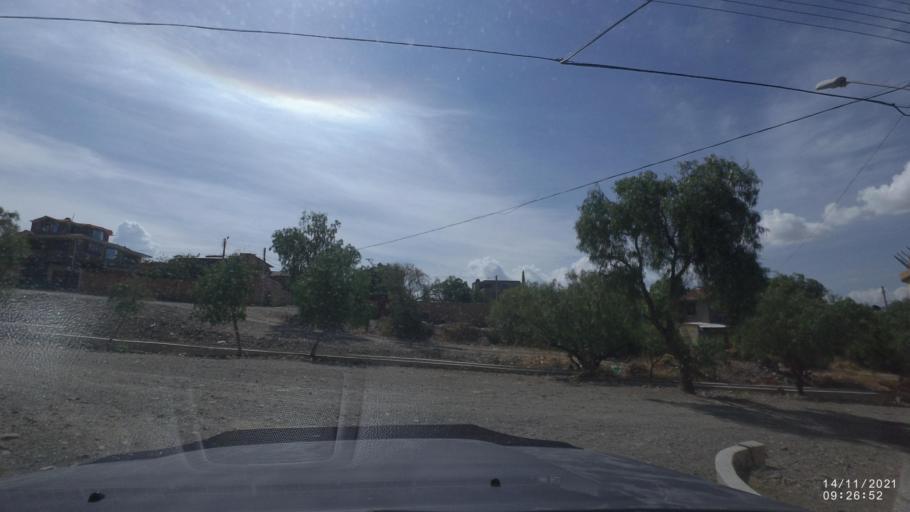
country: BO
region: Cochabamba
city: Cochabamba
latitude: -17.3736
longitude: -66.0928
